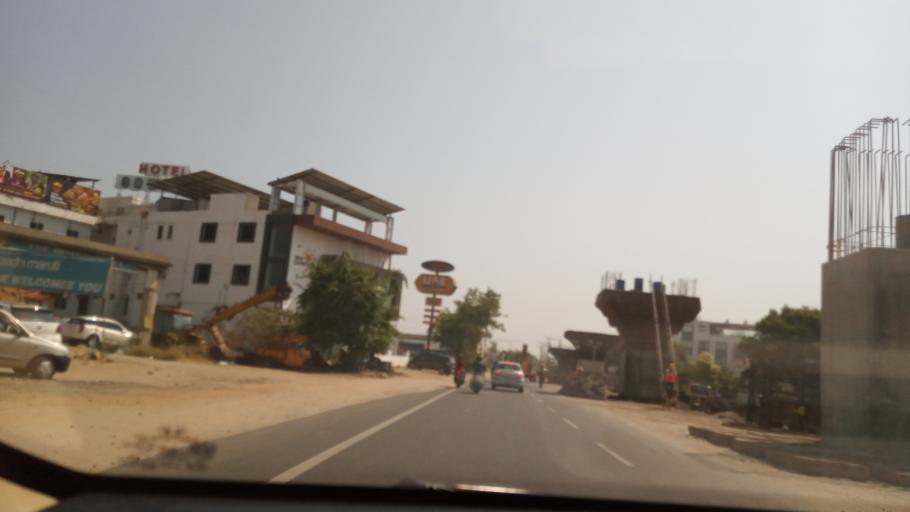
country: IN
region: Tamil Nadu
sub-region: Coimbatore
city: Irugur
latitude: 11.0419
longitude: 77.0428
